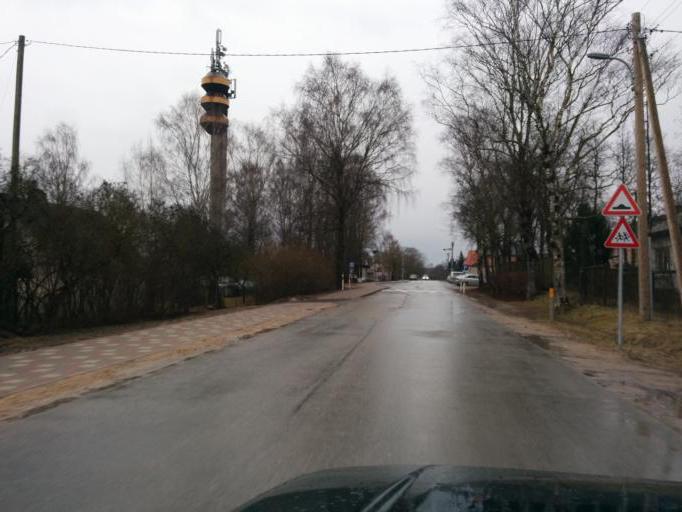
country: LV
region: Kekava
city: Balozi
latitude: 56.8752
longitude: 24.1798
